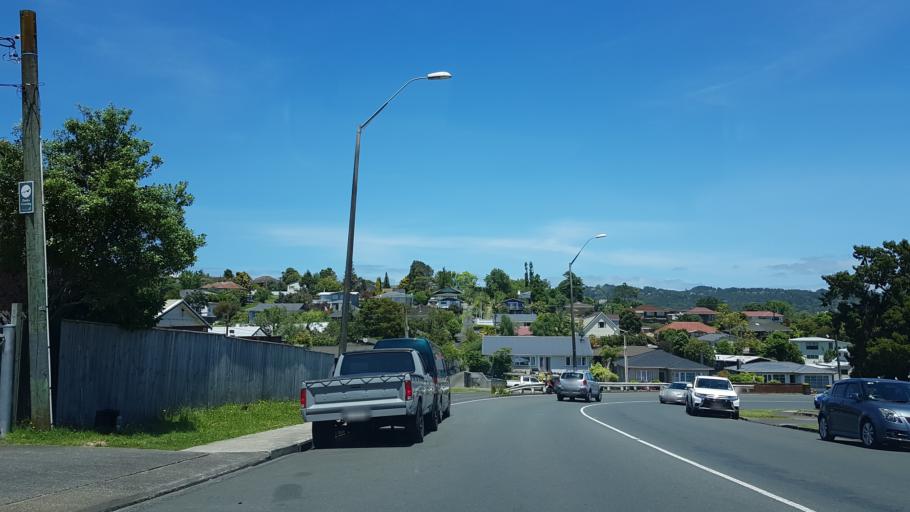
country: NZ
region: Auckland
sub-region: Auckland
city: Waitakere
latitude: -36.9116
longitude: 174.6545
